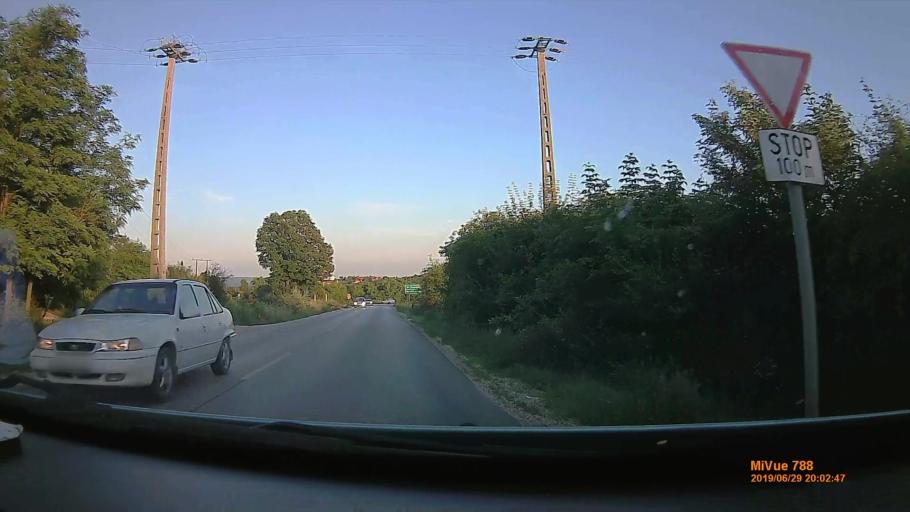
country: HU
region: Pest
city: Zsambek
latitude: 47.5553
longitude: 18.7031
